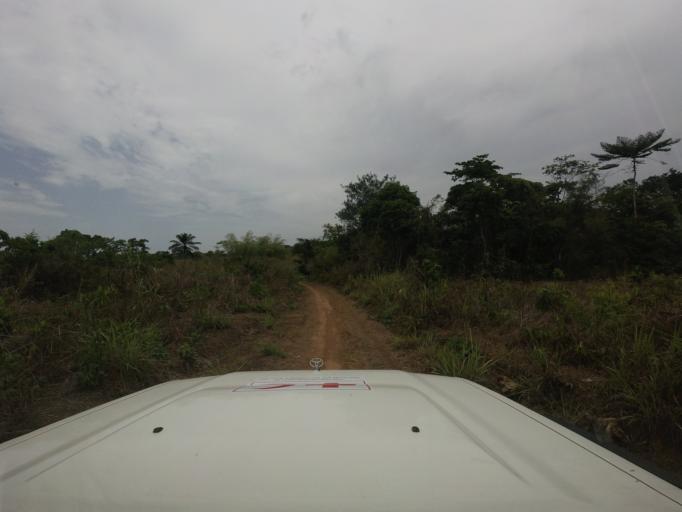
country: SL
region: Eastern Province
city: Buedu
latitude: 8.2493
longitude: -10.2920
